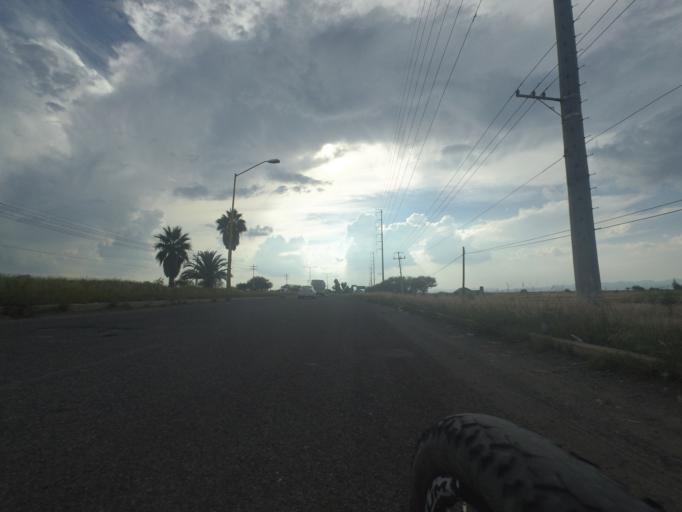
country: MX
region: Aguascalientes
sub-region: Aguascalientes
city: Penuelas (El Cienegal)
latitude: 21.7256
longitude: -102.3022
